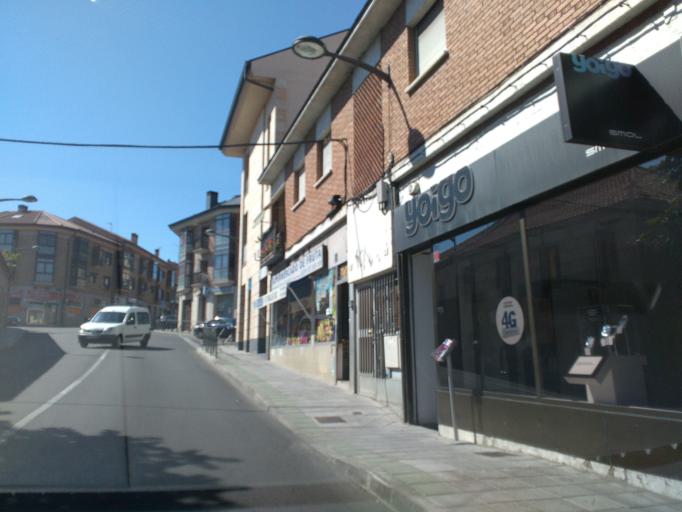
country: ES
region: Madrid
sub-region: Provincia de Madrid
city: Galapagar
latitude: 40.5764
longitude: -4.0028
